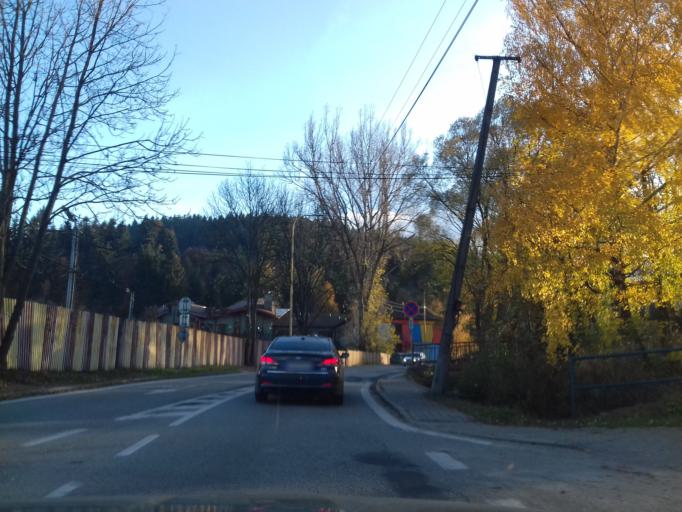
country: SK
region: Zilinsky
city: Ruzomberok
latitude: 49.0826
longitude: 19.2816
